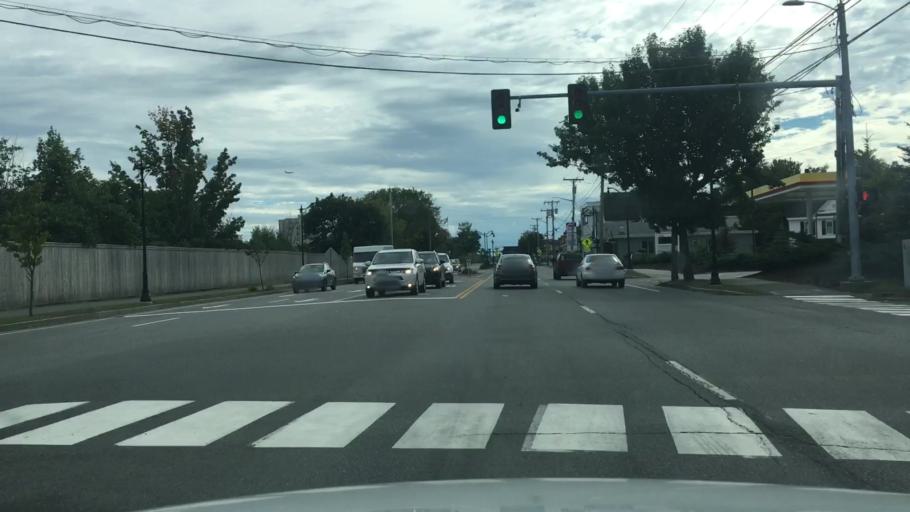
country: US
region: Maine
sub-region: Penobscot County
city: Bangor
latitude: 44.7932
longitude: -68.7755
